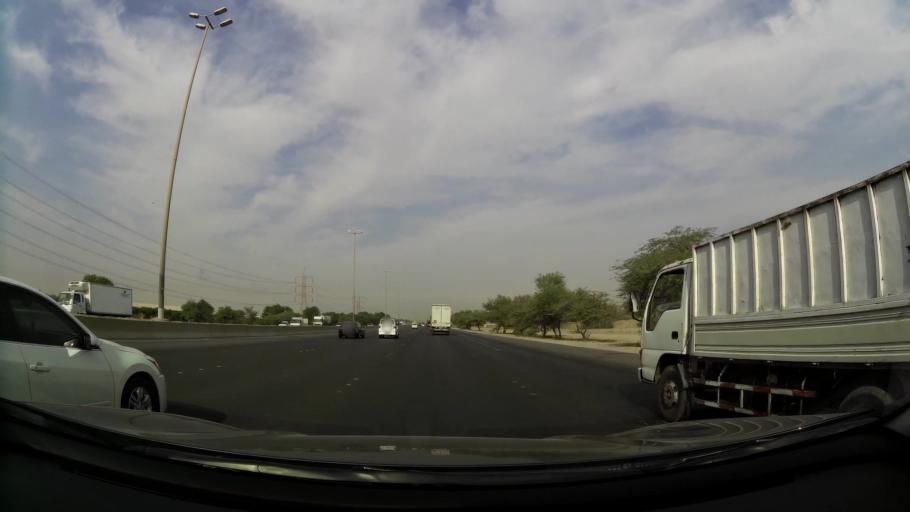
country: KW
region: Al Asimah
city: Ar Rabiyah
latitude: 29.2725
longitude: 47.8157
